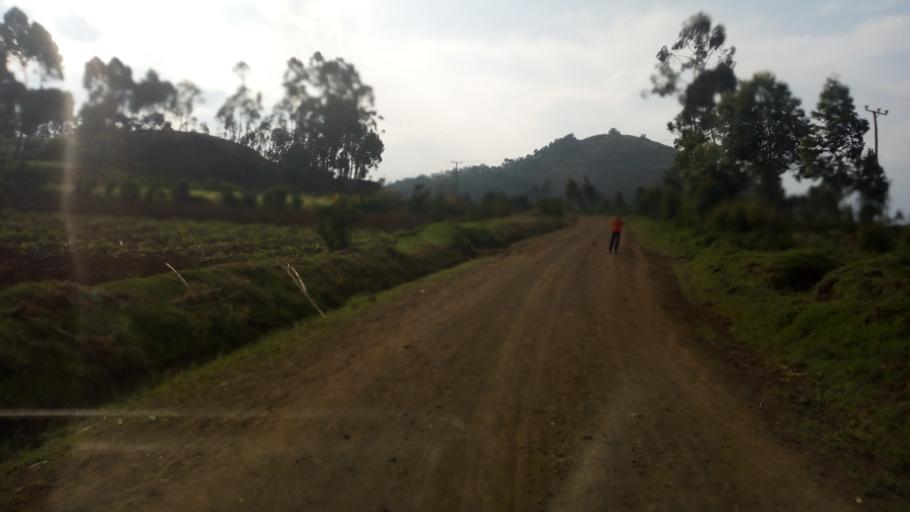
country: UG
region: Western Region
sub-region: Kisoro District
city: Kisoro
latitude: -1.3043
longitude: 29.7094
